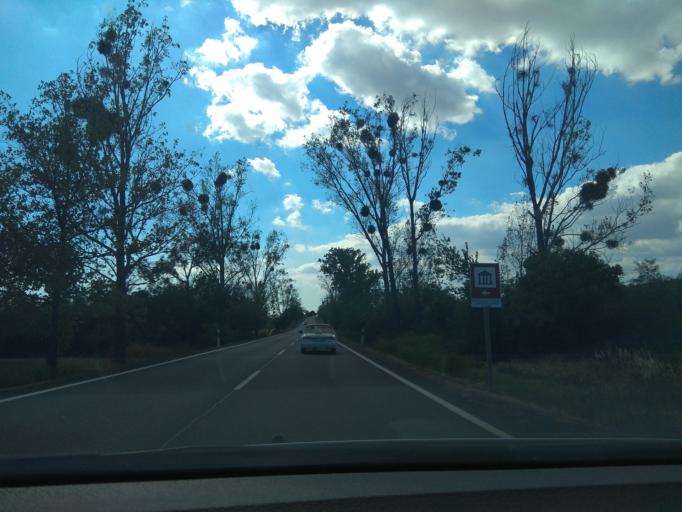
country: HU
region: Borsod-Abauj-Zemplen
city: Tolcsva
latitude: 48.2786
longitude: 21.4952
